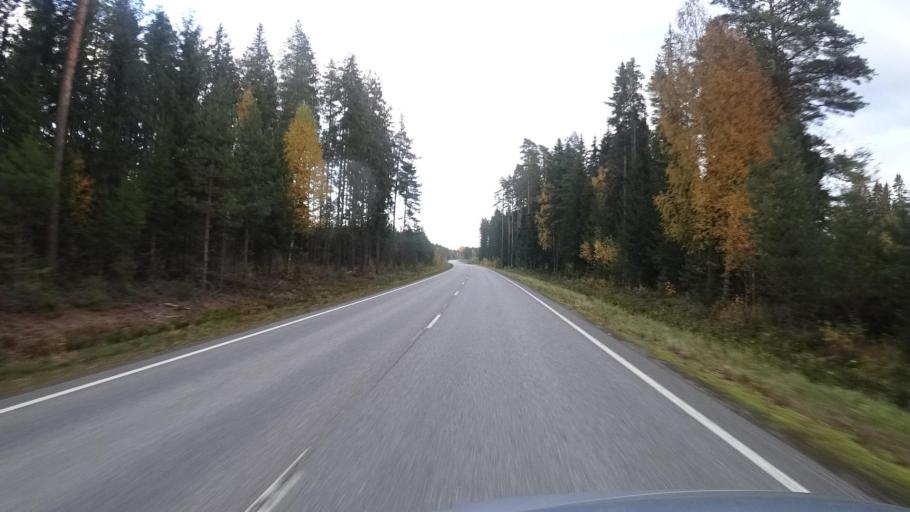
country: FI
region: Varsinais-Suomi
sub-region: Loimaa
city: Ylaene
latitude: 60.9970
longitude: 22.4837
